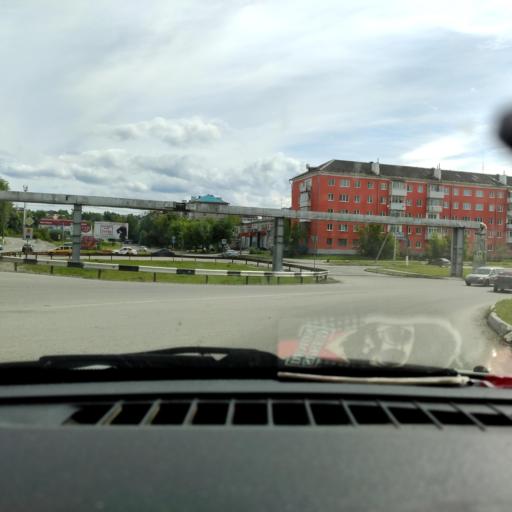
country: RU
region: Perm
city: Chusovoy
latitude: 58.2735
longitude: 57.8160
